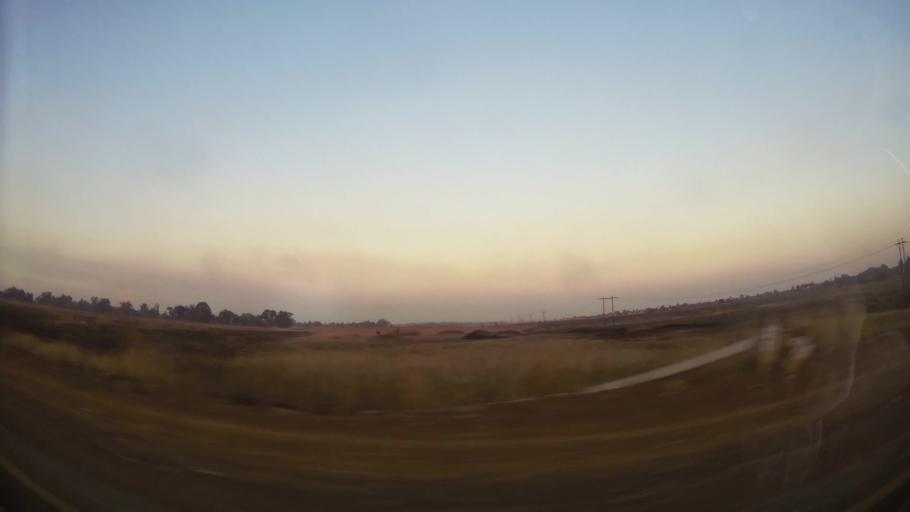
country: ZA
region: Gauteng
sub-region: Ekurhuleni Metropolitan Municipality
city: Springs
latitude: -26.3344
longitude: 28.4220
